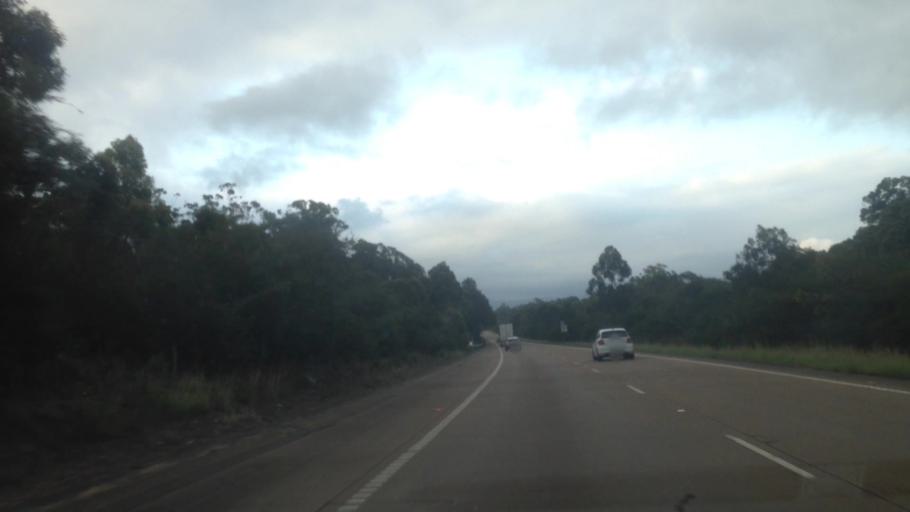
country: AU
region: New South Wales
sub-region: Lake Macquarie Shire
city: Dora Creek
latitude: -33.1376
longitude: 151.4753
